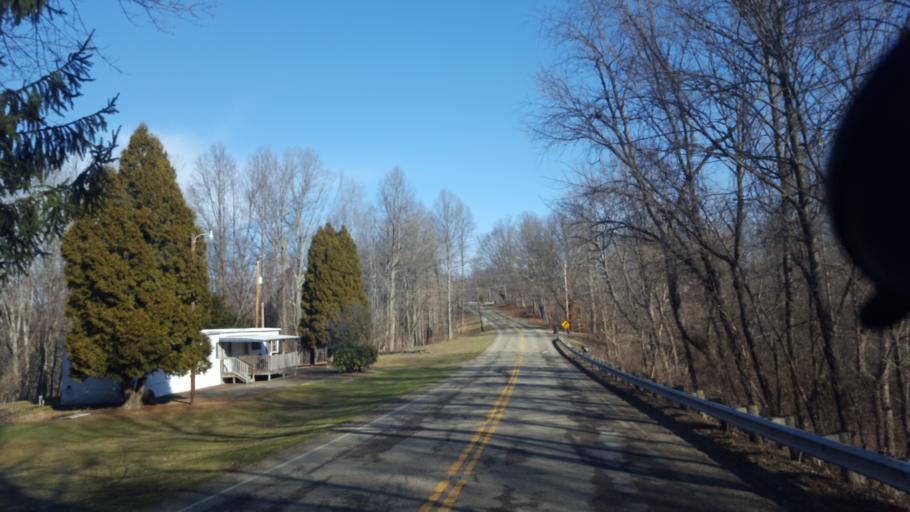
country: US
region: Ohio
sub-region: Guernsey County
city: Cambridge
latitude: 40.1175
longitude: -81.5568
